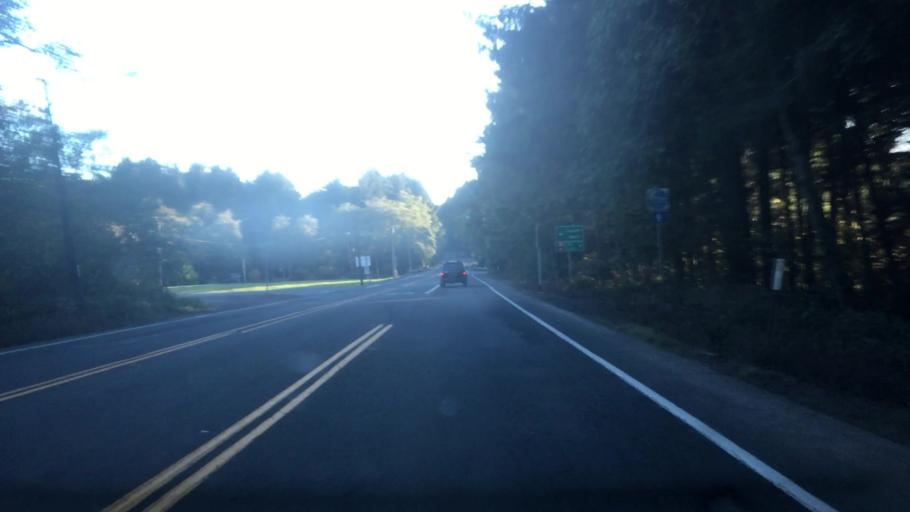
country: US
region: Oregon
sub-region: Clatsop County
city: Cannon Beach
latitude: 45.8894
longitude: -123.9575
